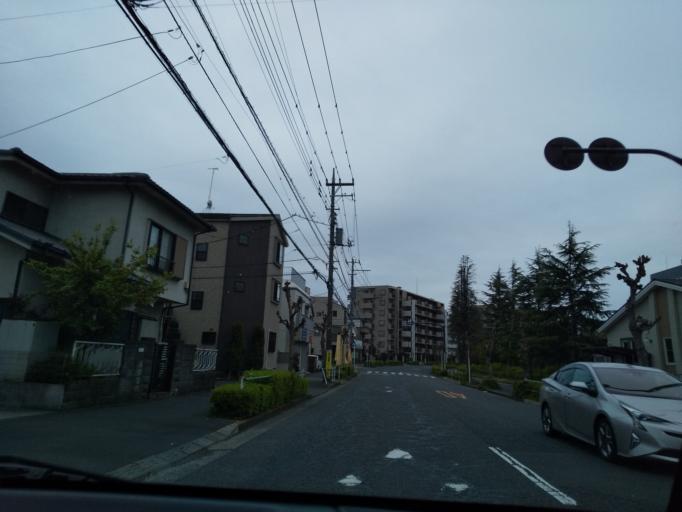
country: JP
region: Tokyo
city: Hino
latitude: 35.6559
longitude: 139.3720
